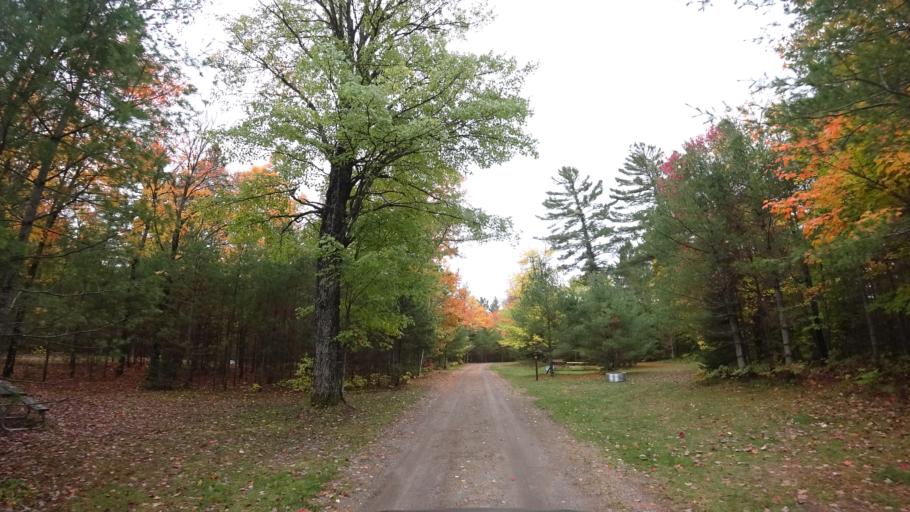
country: US
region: Michigan
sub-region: Marquette County
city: West Ishpeming
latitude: 46.5308
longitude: -88.0003
